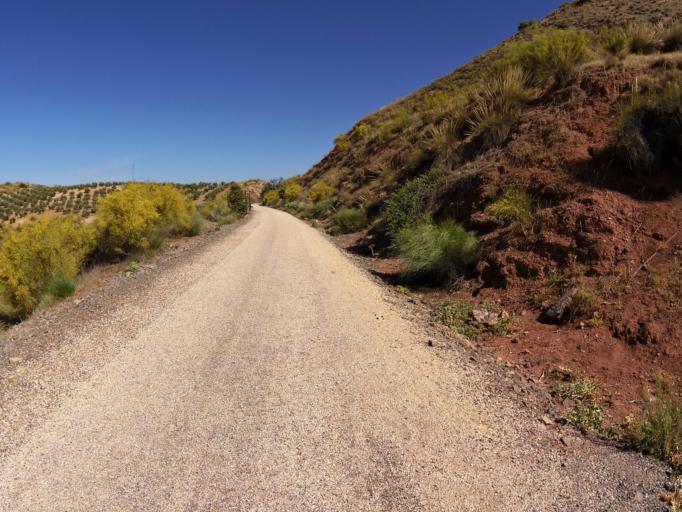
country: ES
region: Andalusia
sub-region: Provincia de Jaen
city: Alcaudete
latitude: 37.5999
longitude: -4.1571
